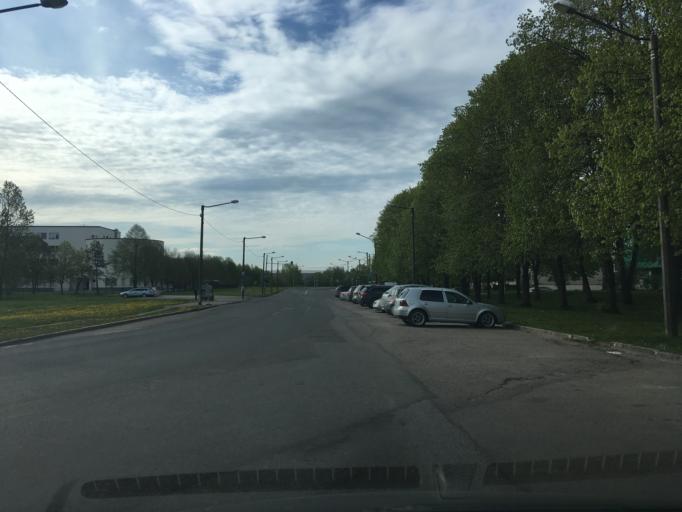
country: EE
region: Harju
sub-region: Tallinna linn
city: Kose
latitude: 59.4394
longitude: 24.8506
